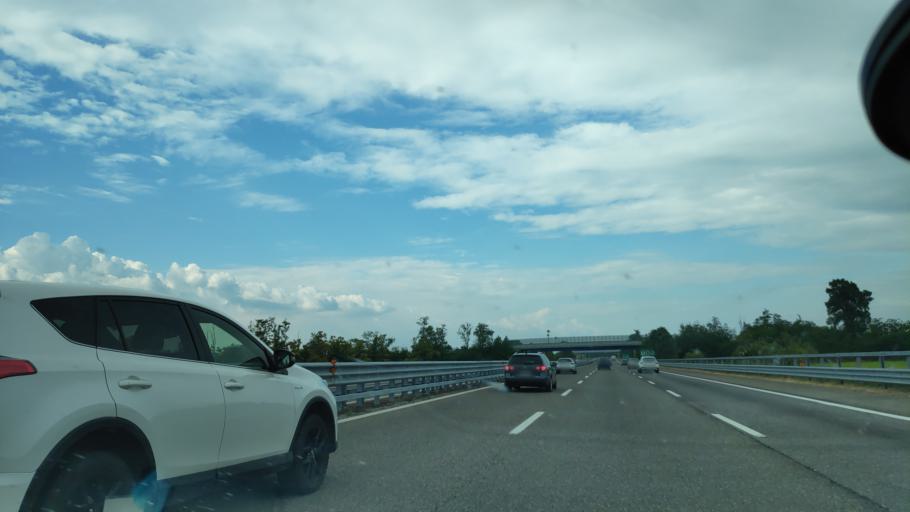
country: IT
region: Lombardy
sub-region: Provincia di Pavia
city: Gropello Cairoli
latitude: 45.1408
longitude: 8.9870
